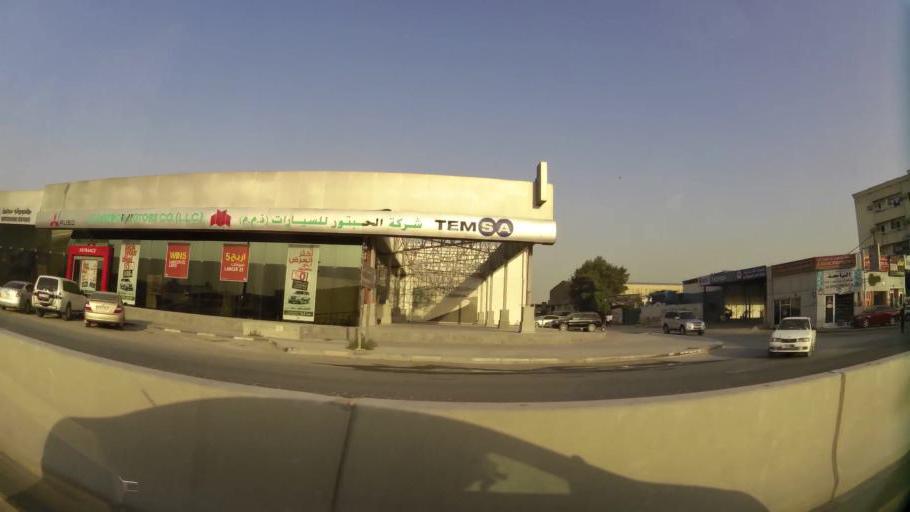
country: AE
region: Ash Shariqah
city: Sharjah
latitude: 25.3290
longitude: 55.4085
